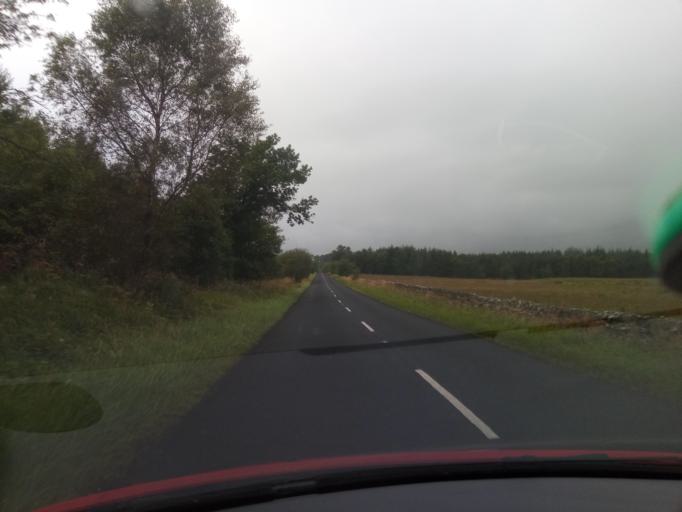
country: GB
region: England
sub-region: Northumberland
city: Rothley
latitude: 55.2015
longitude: -1.9512
